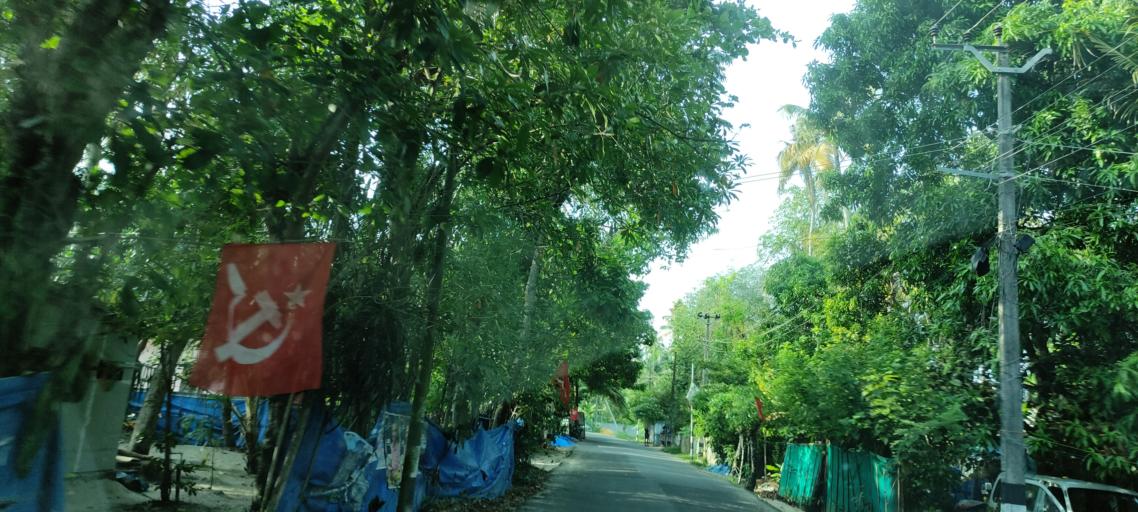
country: IN
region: Kerala
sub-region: Alappuzha
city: Vayalar
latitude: 9.7151
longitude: 76.2880
